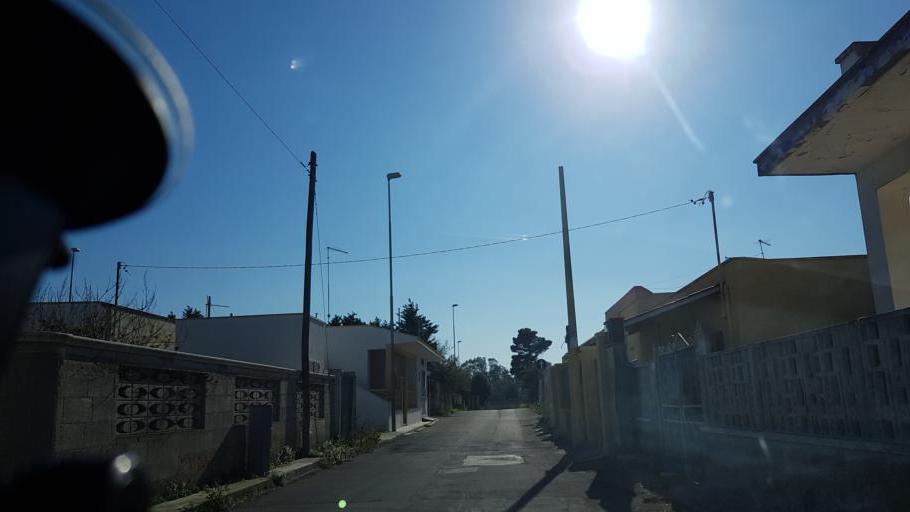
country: IT
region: Apulia
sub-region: Provincia di Brindisi
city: Torchiarolo
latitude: 40.5038
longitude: 18.1143
